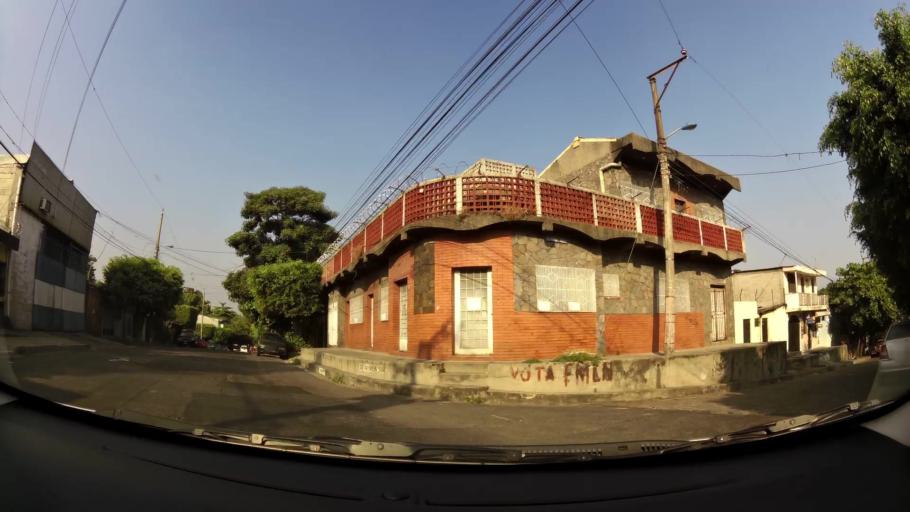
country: SV
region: San Salvador
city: San Salvador
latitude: 13.6964
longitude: -89.1820
